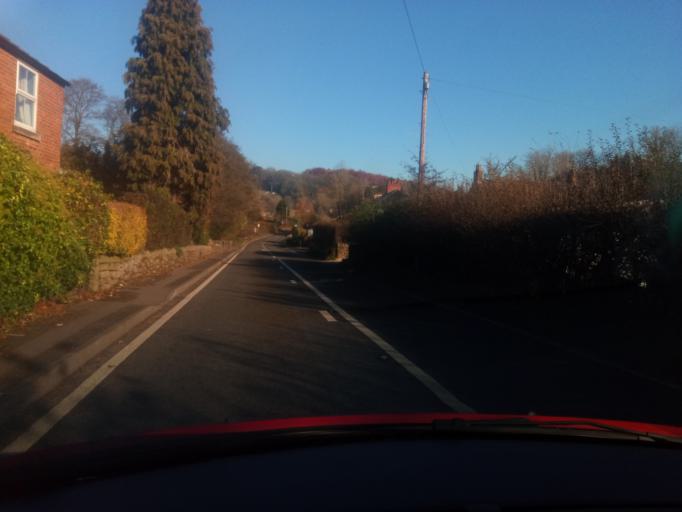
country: GB
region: England
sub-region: Derbyshire
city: Belper
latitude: 53.0254
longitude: -1.5098
